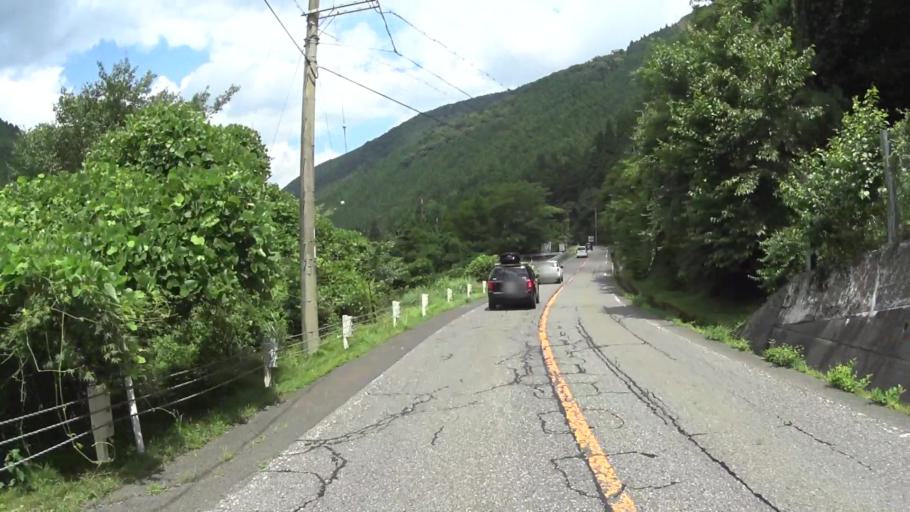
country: JP
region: Shiga Prefecture
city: Kitahama
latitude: 35.1923
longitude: 135.8591
